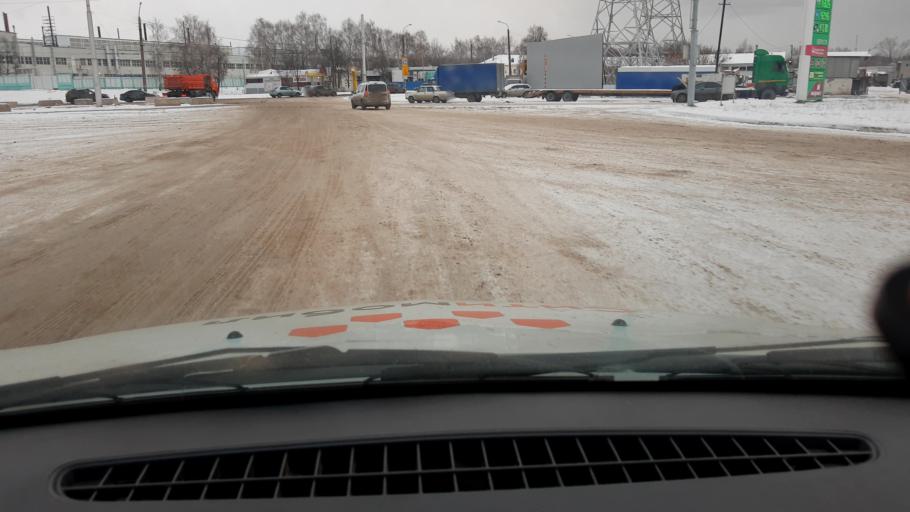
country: RU
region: Bashkortostan
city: Ufa
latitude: 54.7876
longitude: 56.1401
